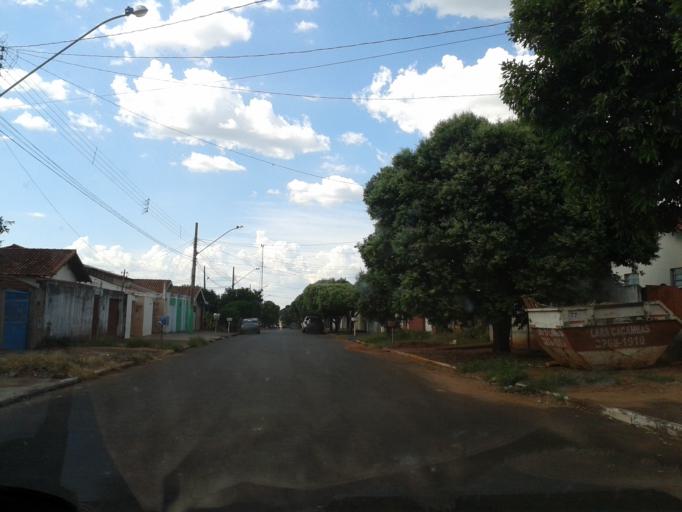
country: BR
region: Minas Gerais
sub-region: Ituiutaba
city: Ituiutaba
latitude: -18.9900
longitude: -49.4686
